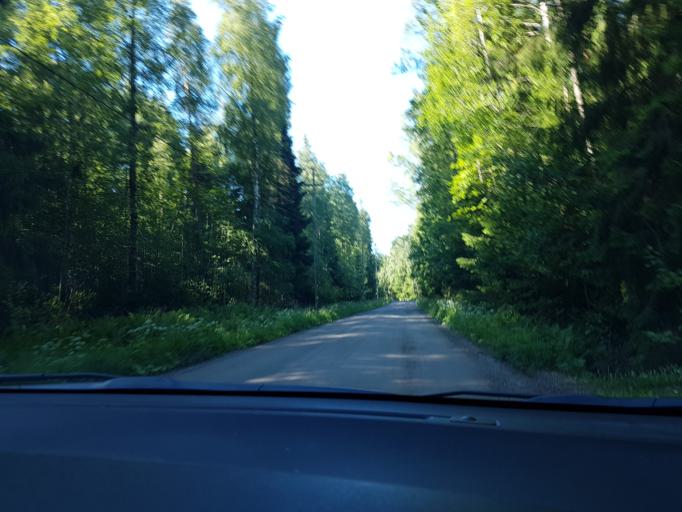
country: FI
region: Uusimaa
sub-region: Helsinki
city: Sibbo
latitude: 60.2657
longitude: 25.2276
